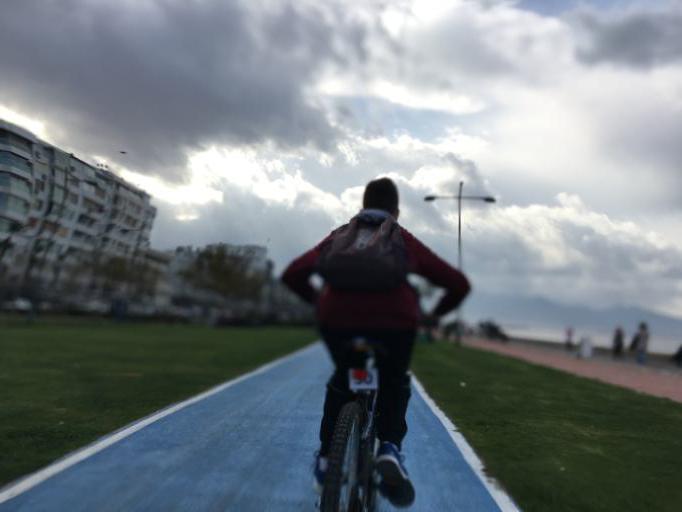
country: TR
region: Izmir
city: Izmir
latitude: 38.4348
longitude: 27.1385
